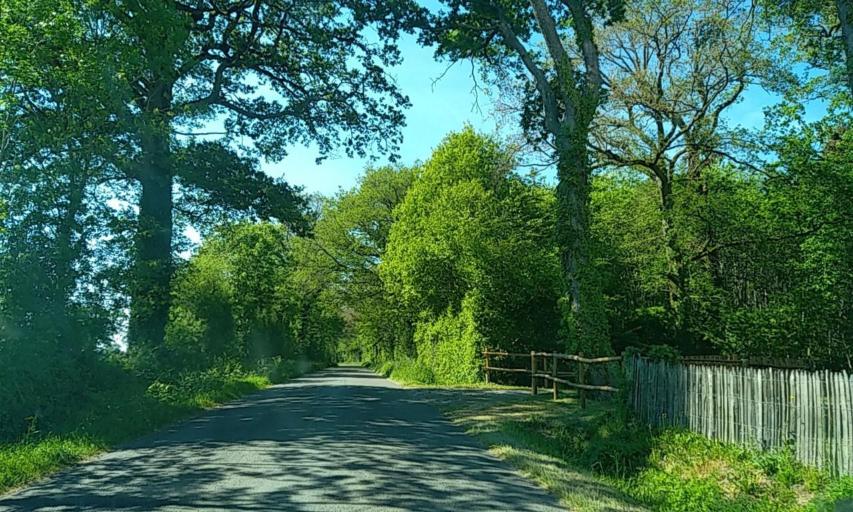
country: FR
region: Poitou-Charentes
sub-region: Departement des Deux-Sevres
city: Boisme
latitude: 46.7991
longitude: -0.4547
